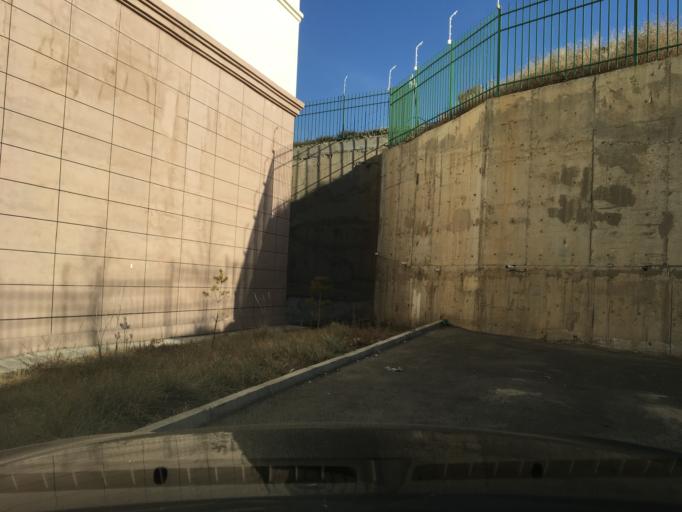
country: MN
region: Ulaanbaatar
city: Ulaanbaatar
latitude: 47.8752
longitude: 106.9180
